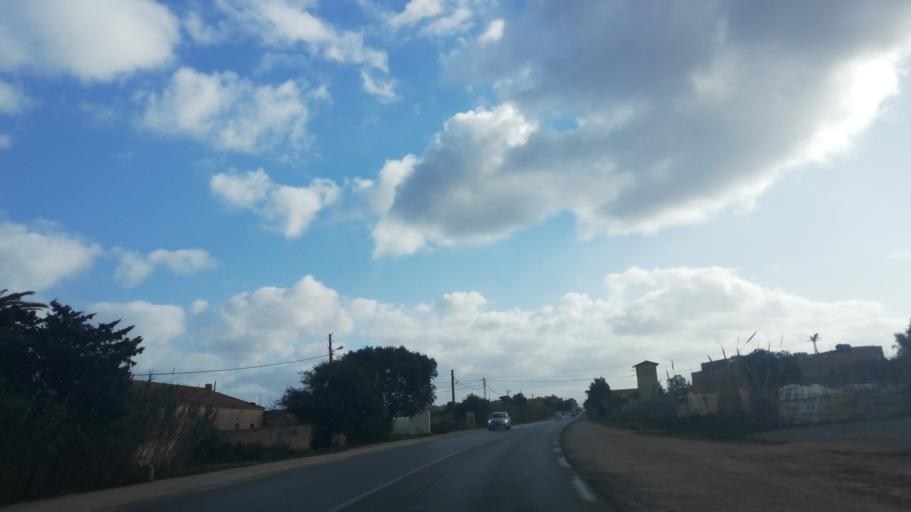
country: DZ
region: Relizane
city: Mazouna
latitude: 36.2475
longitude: 0.5416
